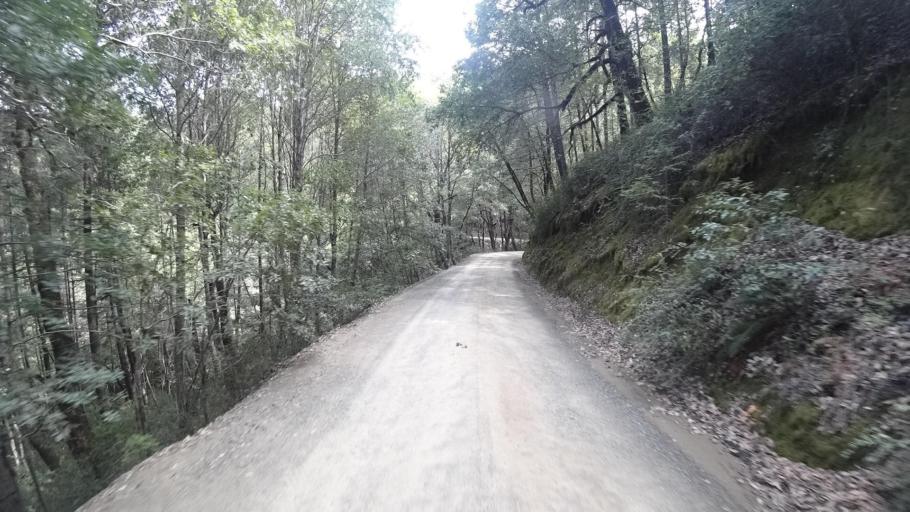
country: US
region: California
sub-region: Humboldt County
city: Redway
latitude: 40.0301
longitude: -123.8358
